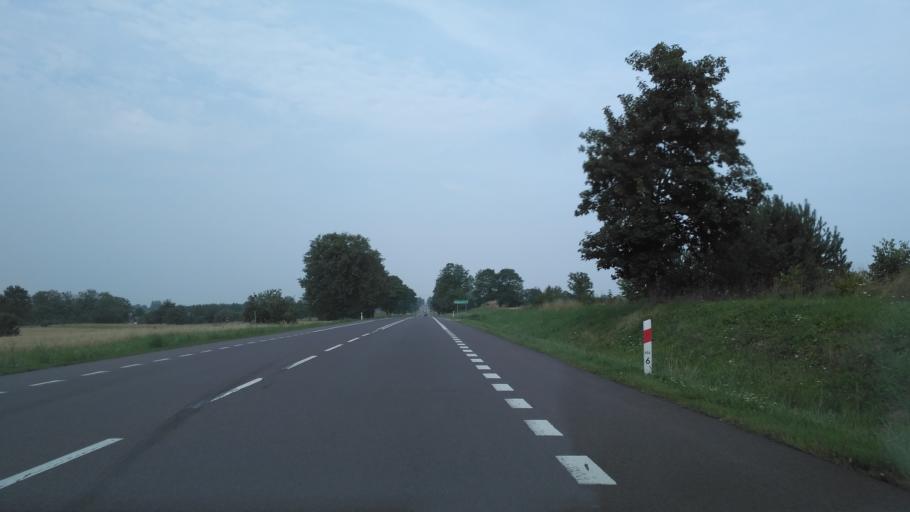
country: PL
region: Lublin Voivodeship
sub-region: Powiat chelmski
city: Rejowiec Fabryczny
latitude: 51.1747
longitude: 23.1631
